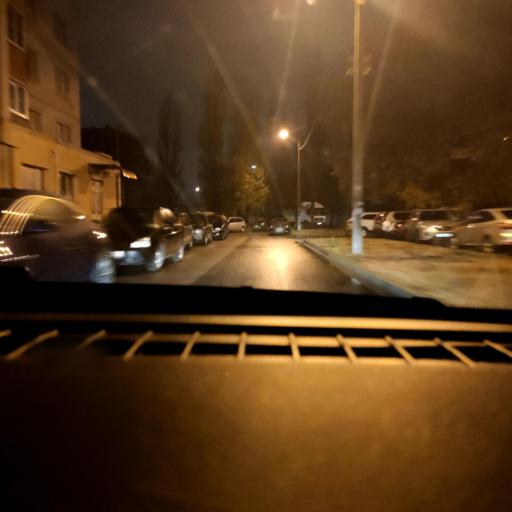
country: RU
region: Voronezj
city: Voronezh
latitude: 51.6356
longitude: 39.2615
